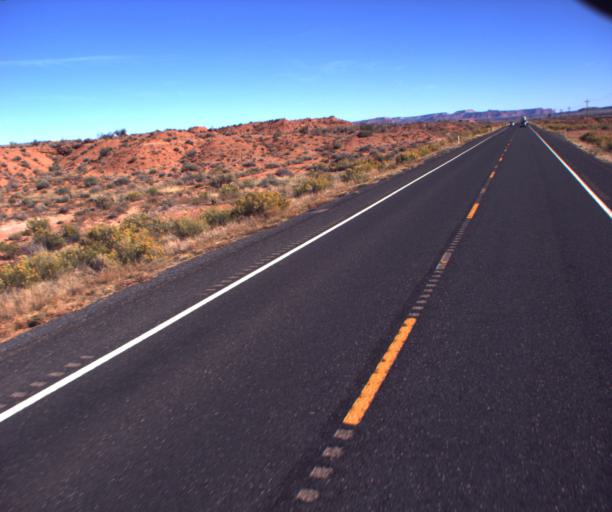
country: US
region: Arizona
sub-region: Coconino County
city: Fredonia
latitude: 36.9135
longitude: -112.5830
